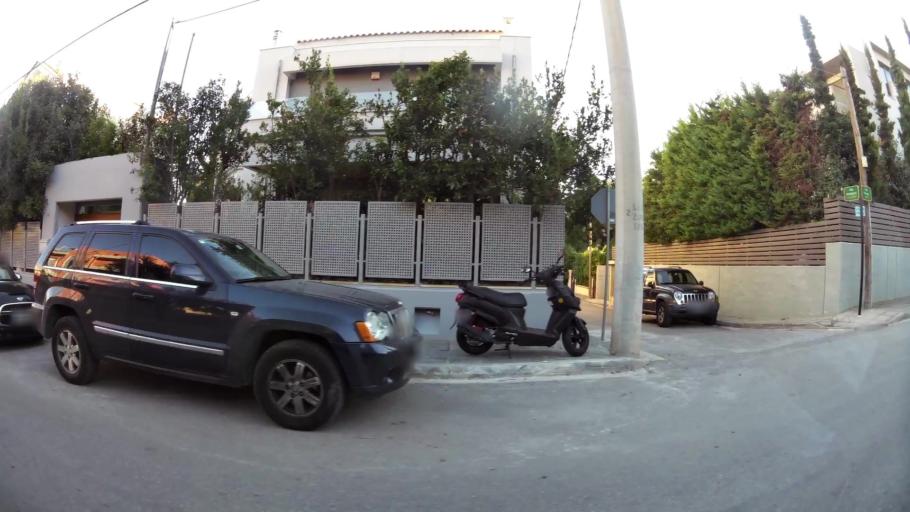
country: GR
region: Attica
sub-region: Nomarchia Anatolikis Attikis
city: Vari
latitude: 37.8281
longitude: 23.7945
